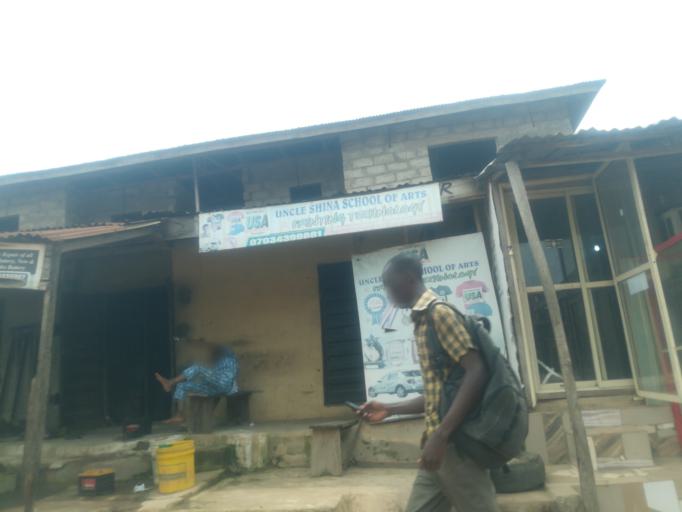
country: NG
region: Oyo
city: Ibadan
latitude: 7.4271
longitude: 3.9335
